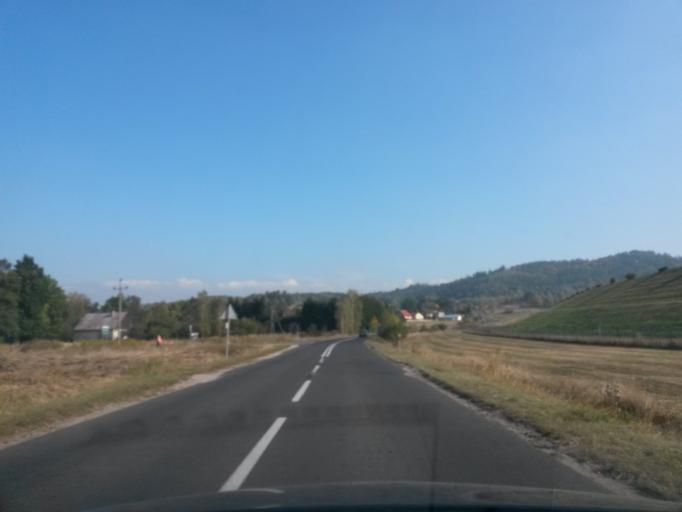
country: PL
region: Lower Silesian Voivodeship
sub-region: Powiat jeleniogorski
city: Podgorzyn
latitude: 50.8319
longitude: 15.7015
